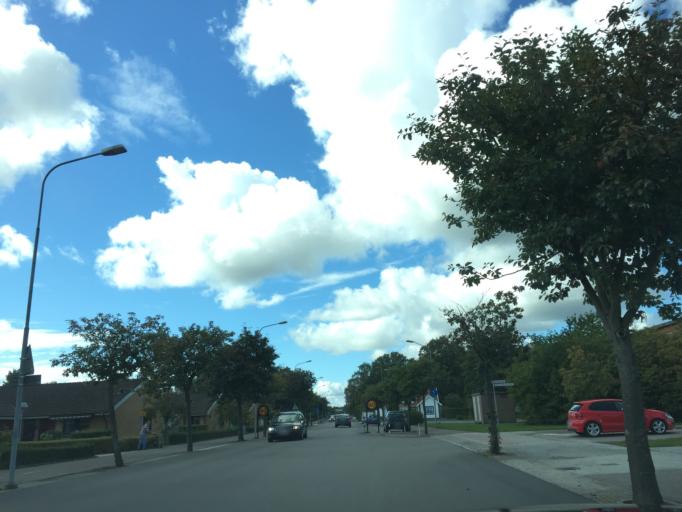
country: SE
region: Skane
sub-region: Sjobo Kommun
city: Sjoebo
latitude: 55.6338
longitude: 13.6941
